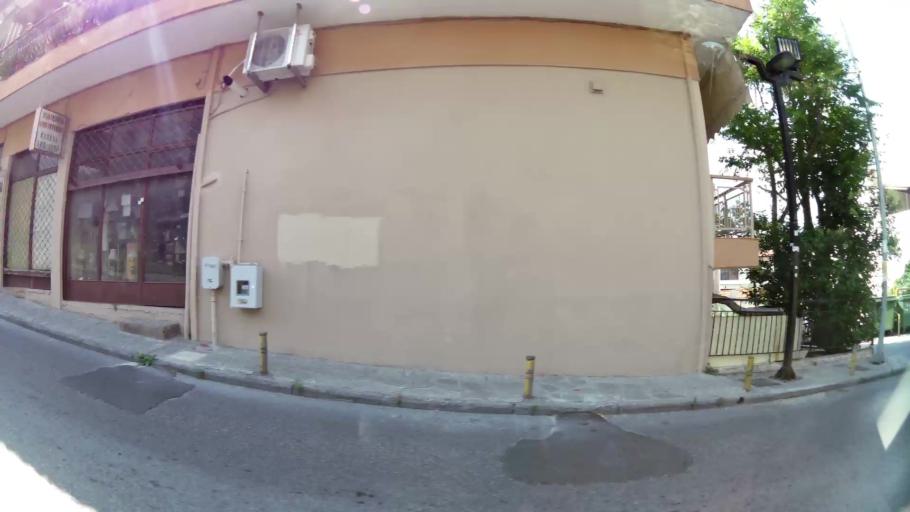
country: GR
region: Central Macedonia
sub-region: Nomos Thessalonikis
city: Agios Pavlos
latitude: 40.6425
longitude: 22.9622
